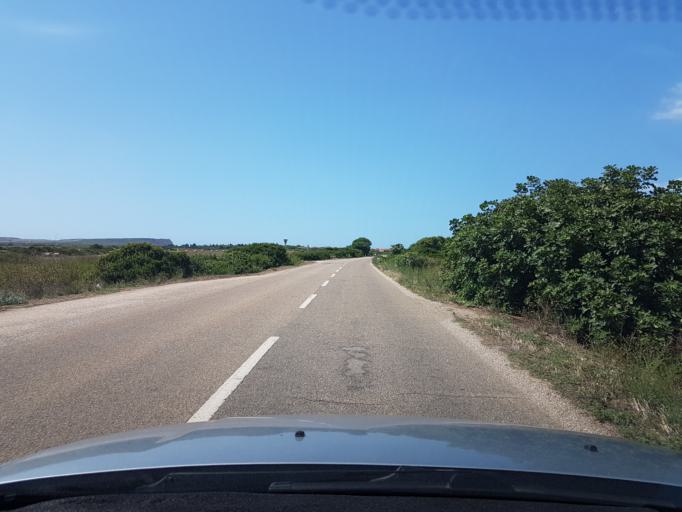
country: IT
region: Sardinia
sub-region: Provincia di Oristano
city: Riola Sardo
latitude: 40.0339
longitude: 8.4239
